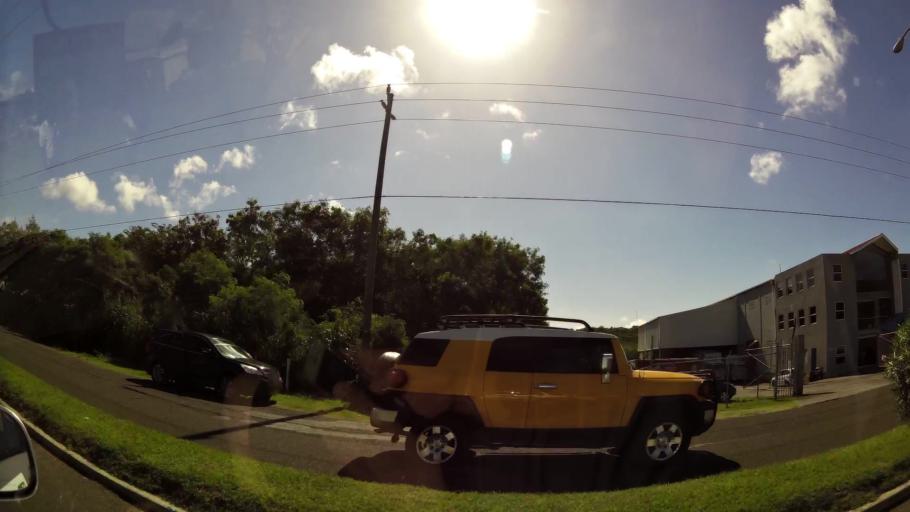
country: GD
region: Saint George
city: Saint George's
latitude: 12.0107
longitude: -61.7644
